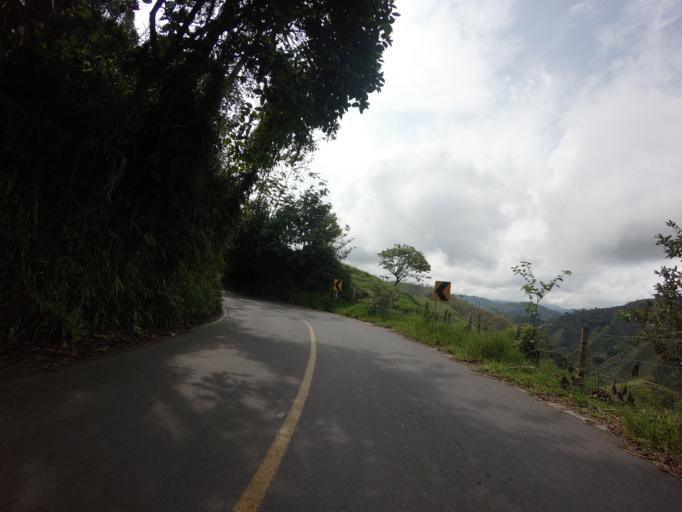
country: CO
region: Caldas
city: Marquetalia
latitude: 5.2992
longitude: -75.0371
